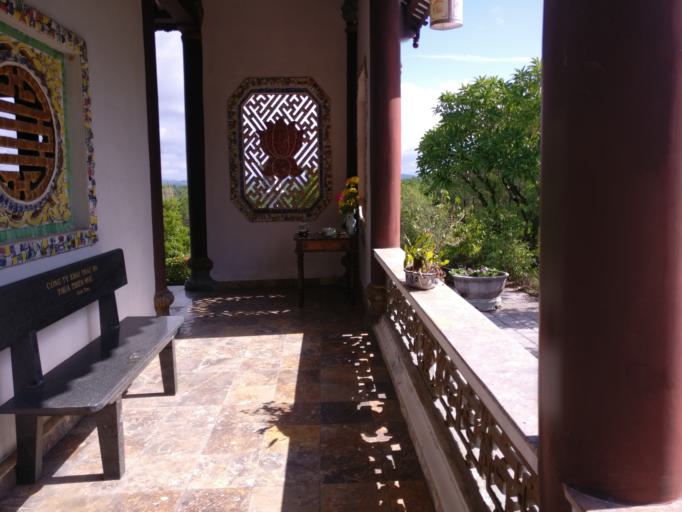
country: VN
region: Thua Thien-Hue
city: Hue
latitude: 16.4211
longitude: 107.6083
